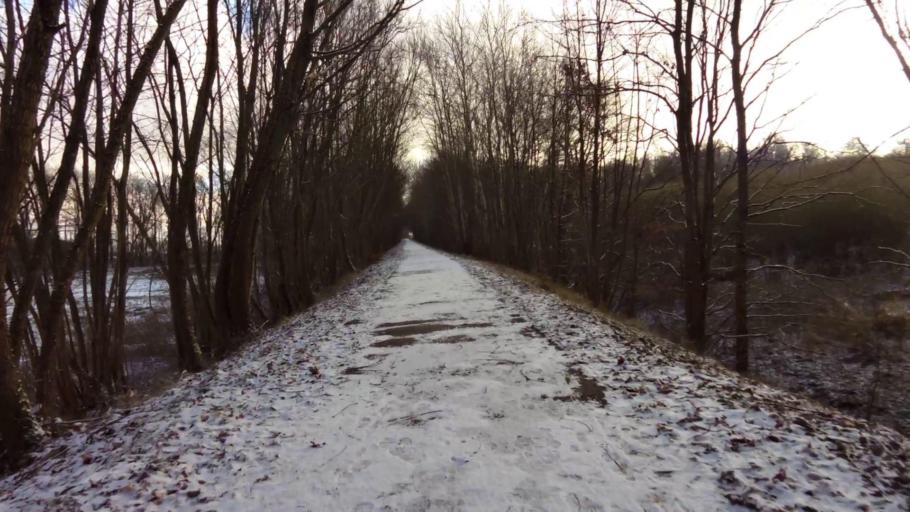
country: PL
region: West Pomeranian Voivodeship
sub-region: Powiat swidwinski
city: Polczyn-Zdroj
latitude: 53.7523
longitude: 16.0582
